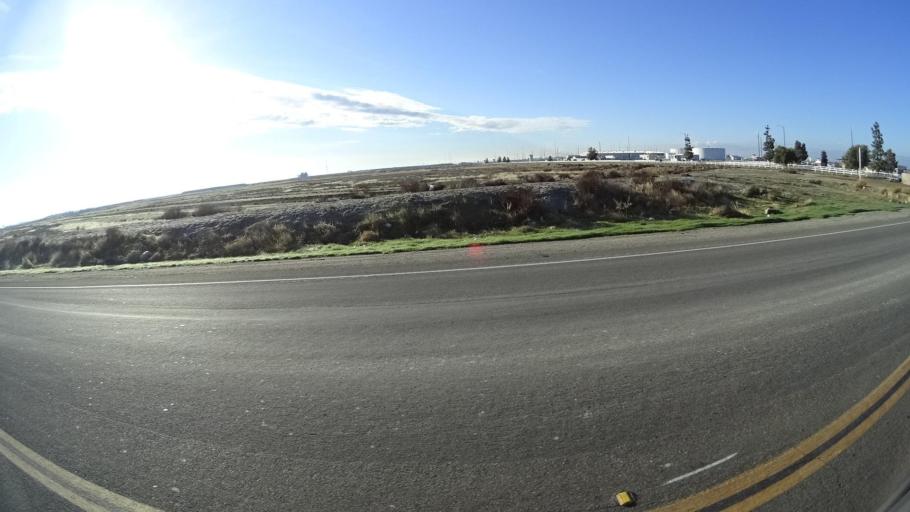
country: US
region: California
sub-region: Kern County
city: Delano
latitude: 35.7759
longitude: -119.3201
